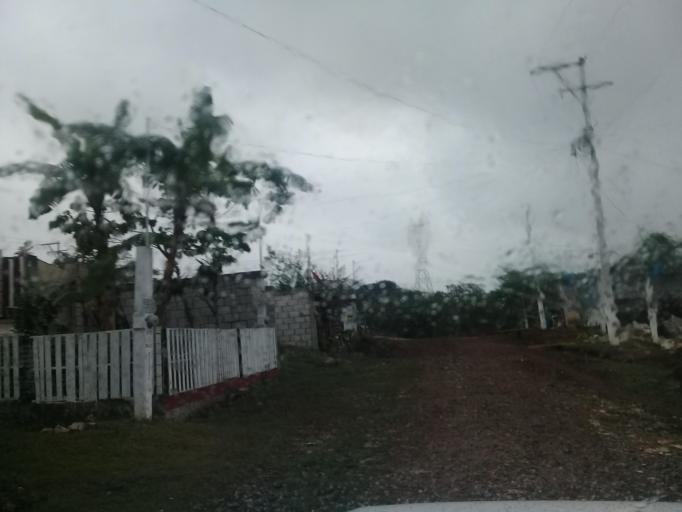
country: MX
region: Veracruz
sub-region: Cordoba
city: Veinte de Noviembre
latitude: 18.8575
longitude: -96.9569
